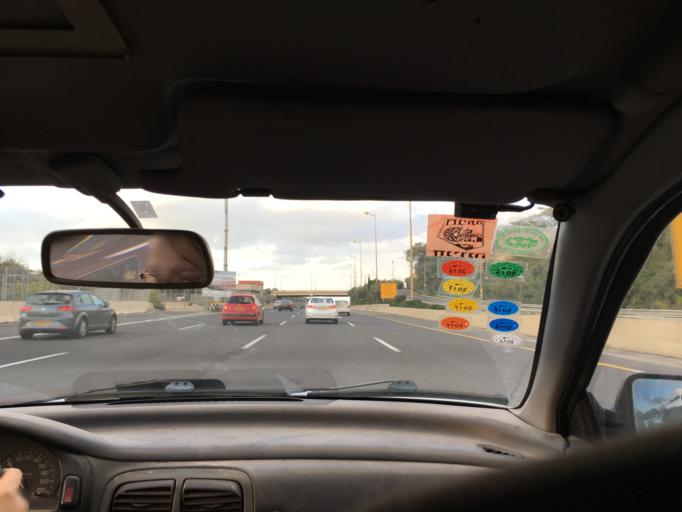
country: IL
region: Tel Aviv
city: Ramat Gan
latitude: 32.1157
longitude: 34.8110
